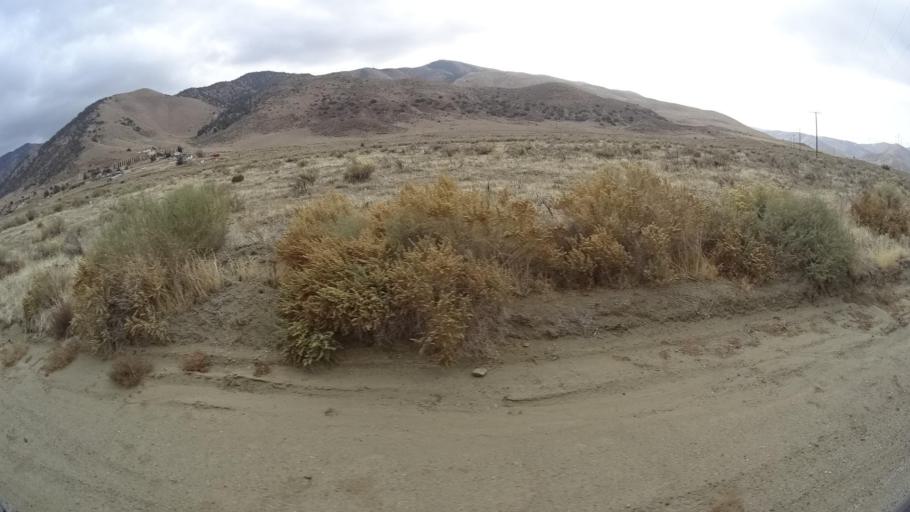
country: US
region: California
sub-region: Kern County
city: Tehachapi
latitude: 35.1402
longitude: -118.3177
